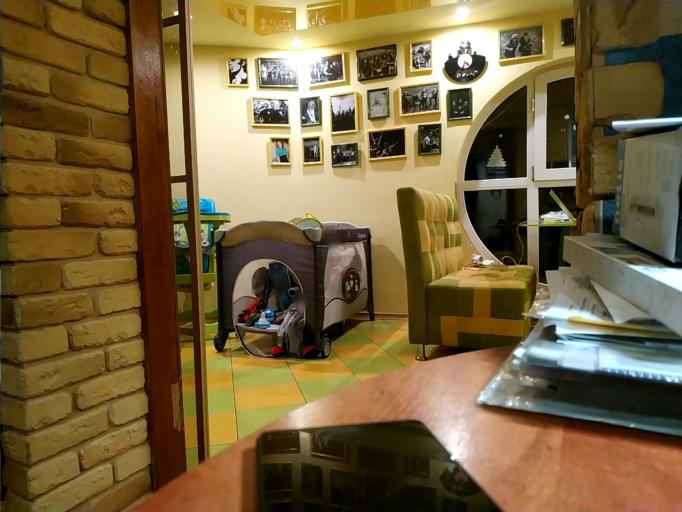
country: RU
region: Orjol
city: Naryshkino
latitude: 53.0097
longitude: 35.6935
